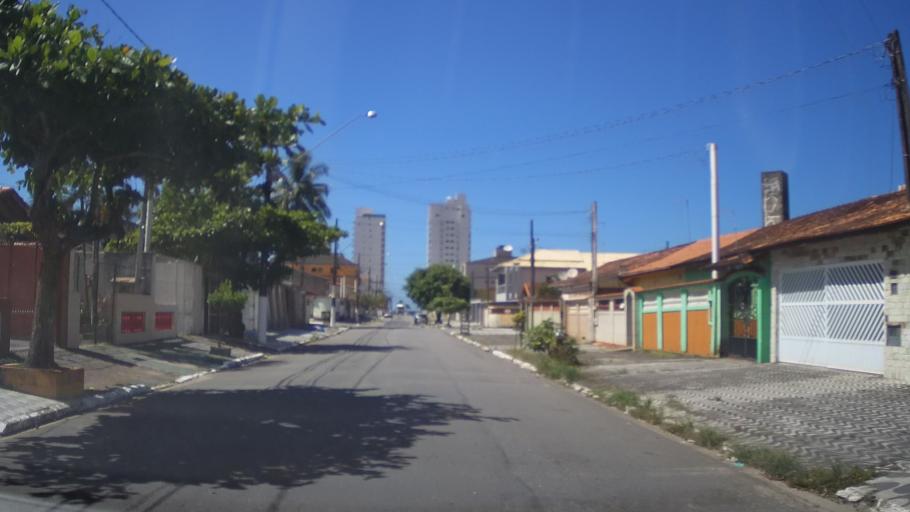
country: BR
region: Sao Paulo
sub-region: Mongagua
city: Mongagua
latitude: -24.0425
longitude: -46.5147
